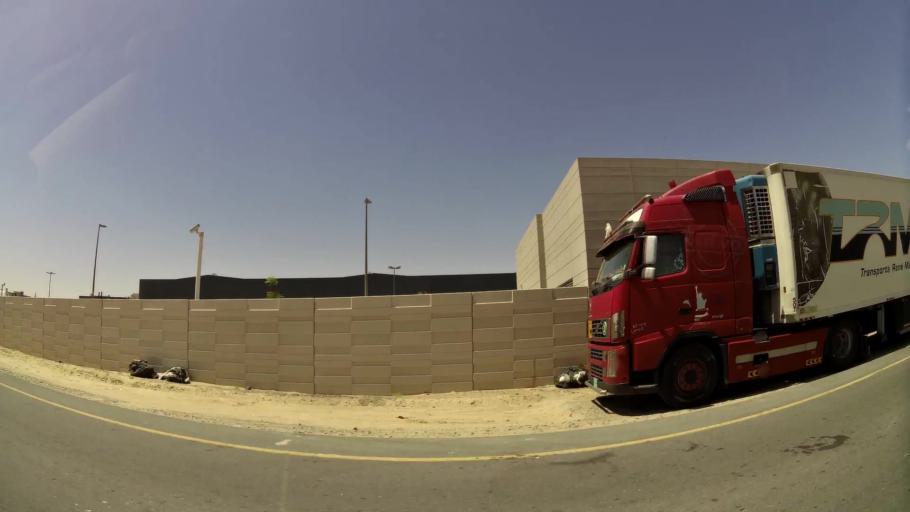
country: AE
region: Dubai
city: Dubai
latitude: 24.9768
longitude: 55.1969
